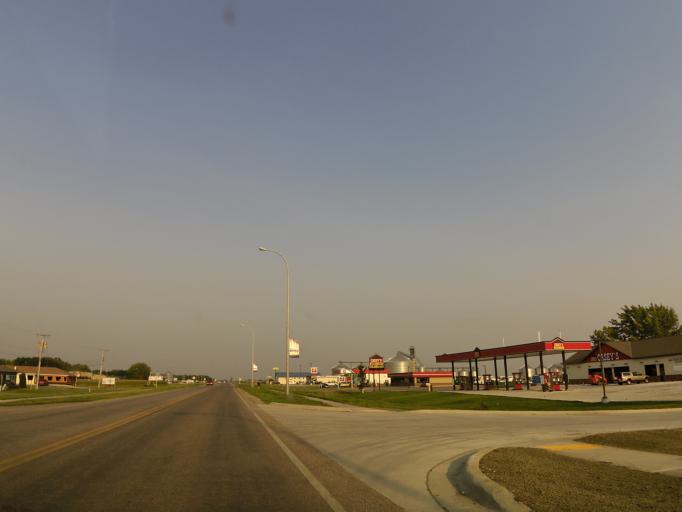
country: US
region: North Dakota
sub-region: Traill County
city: Mayville
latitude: 47.4980
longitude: -97.3145
